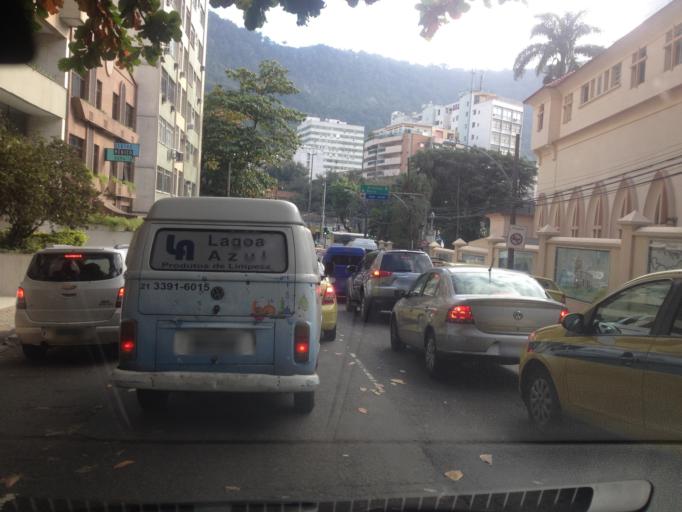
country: BR
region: Rio de Janeiro
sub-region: Rio De Janeiro
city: Rio de Janeiro
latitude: -22.9584
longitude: -43.1988
